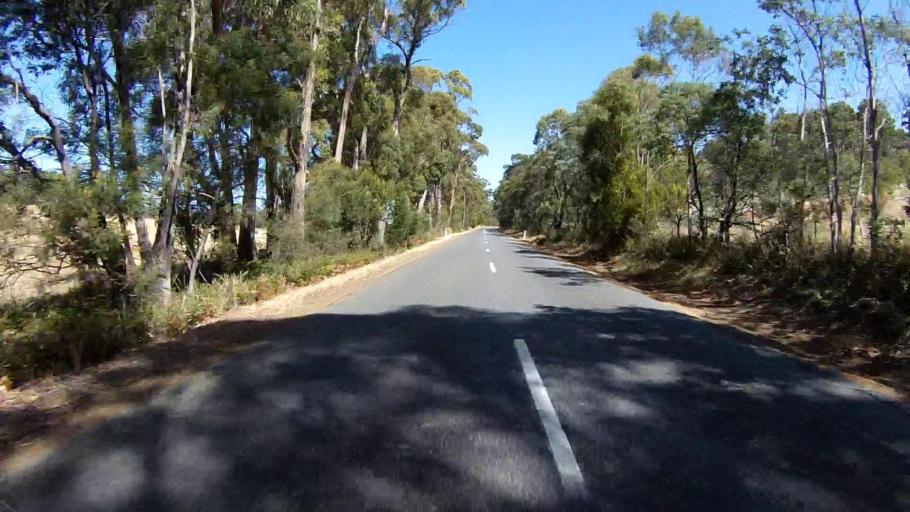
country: AU
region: Tasmania
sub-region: Sorell
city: Sorell
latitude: -42.3130
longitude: 147.9610
